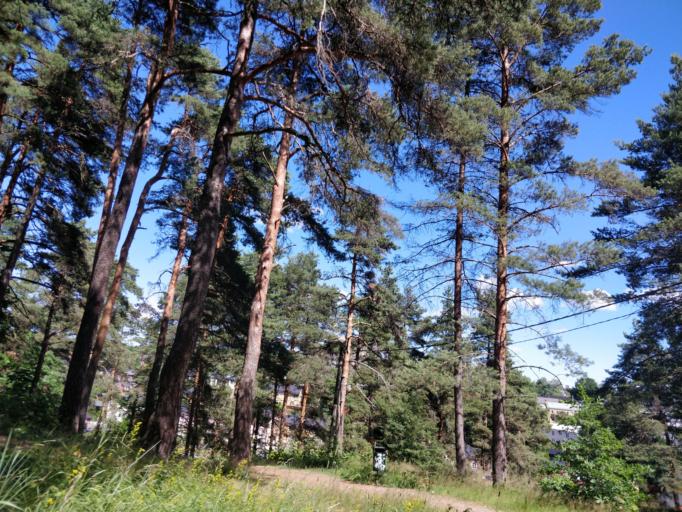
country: FI
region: Uusimaa
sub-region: Porvoo
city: Porvoo
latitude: 60.3951
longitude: 25.6542
